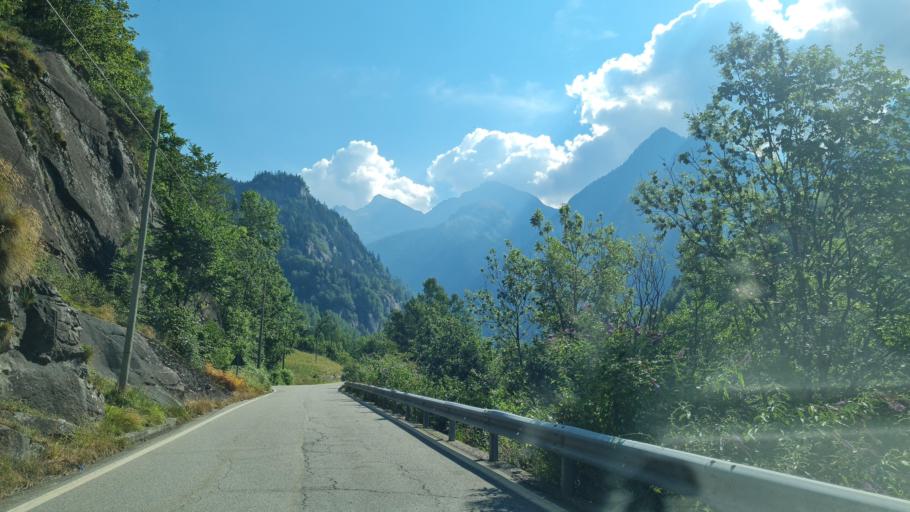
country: IT
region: Piedmont
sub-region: Provincia Verbano-Cusio-Ossola
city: Formazza
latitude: 46.3302
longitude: 8.3934
